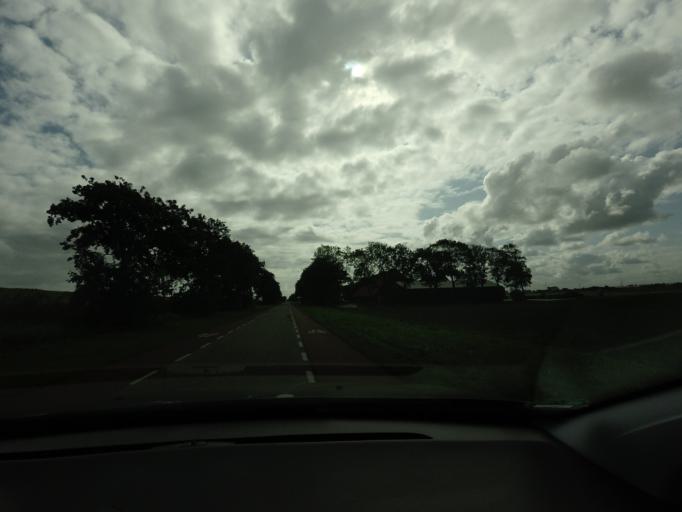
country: NL
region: North Holland
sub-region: Gemeente Hollands Kroon
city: Den Oever
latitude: 52.8694
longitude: 5.0927
